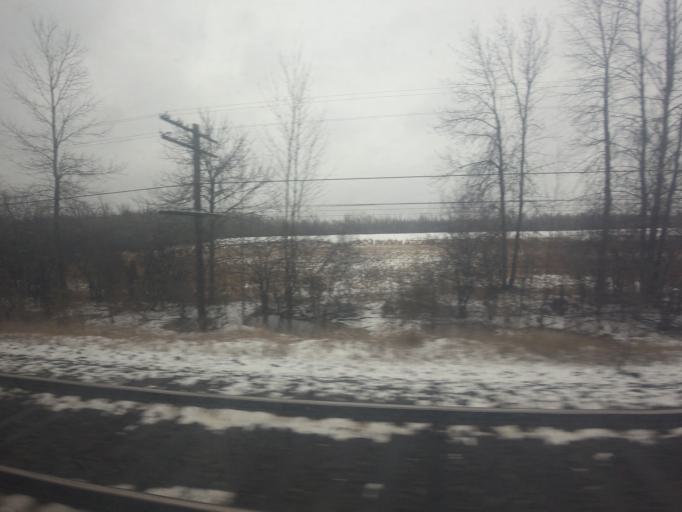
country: CA
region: Ontario
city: Quinte West
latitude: 44.1401
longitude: -77.5208
